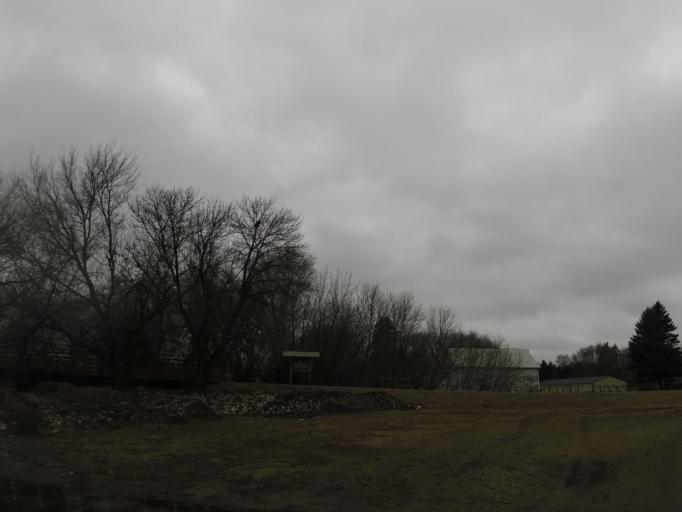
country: US
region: North Dakota
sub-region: Traill County
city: Hillsboro
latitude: 47.1881
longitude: -97.2176
